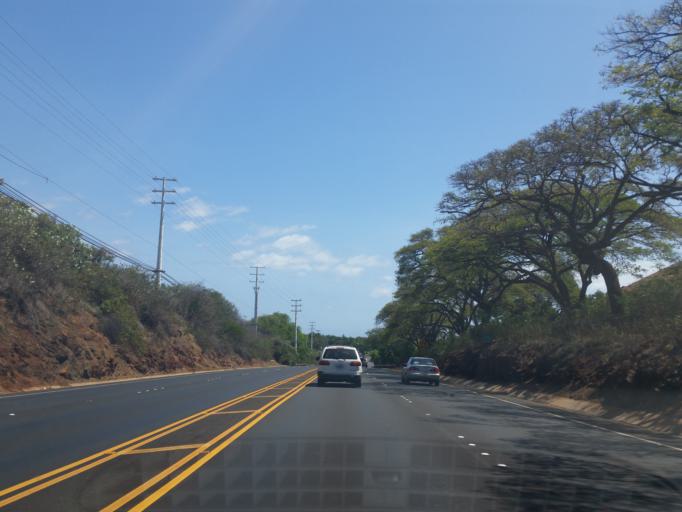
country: US
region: Hawaii
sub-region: Maui County
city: Ka'anapali
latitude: 20.9228
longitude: -156.6901
